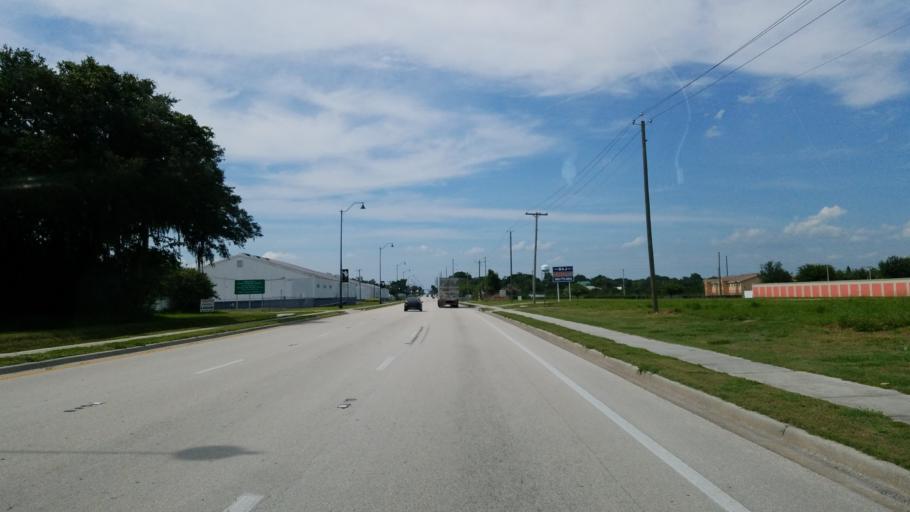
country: US
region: Florida
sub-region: Hardee County
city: Wauchula
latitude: 27.5391
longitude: -81.8084
